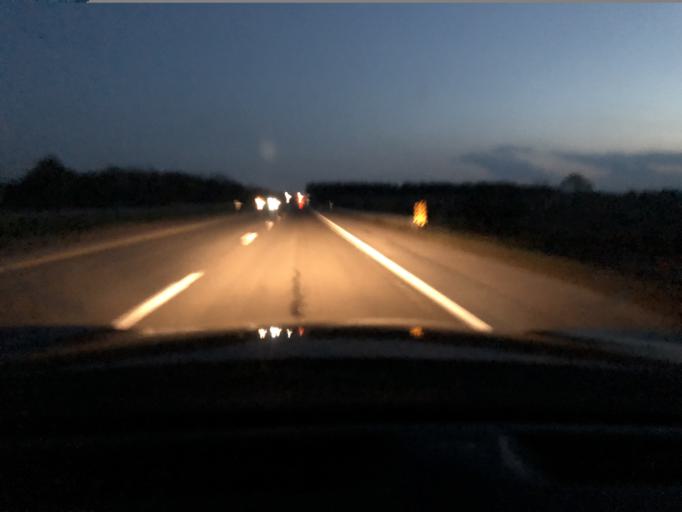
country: US
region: Indiana
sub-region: Steuben County
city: Angola
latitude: 41.5586
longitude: -85.0574
